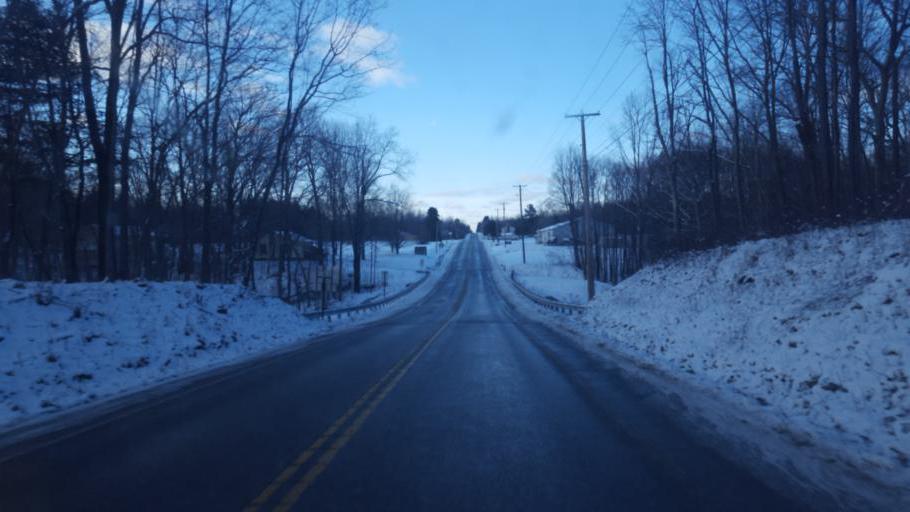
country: US
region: Pennsylvania
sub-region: Mercer County
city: Stoneboro
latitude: 41.3960
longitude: -80.2151
